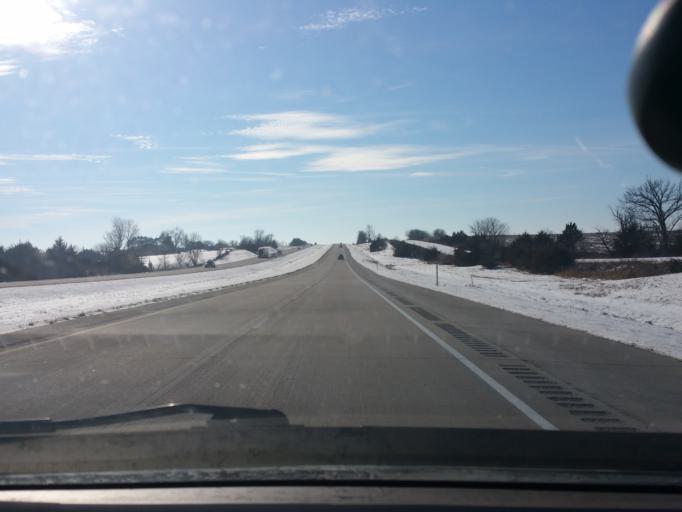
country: US
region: Iowa
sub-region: Decatur County
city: Leon
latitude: 40.7895
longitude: -93.8351
